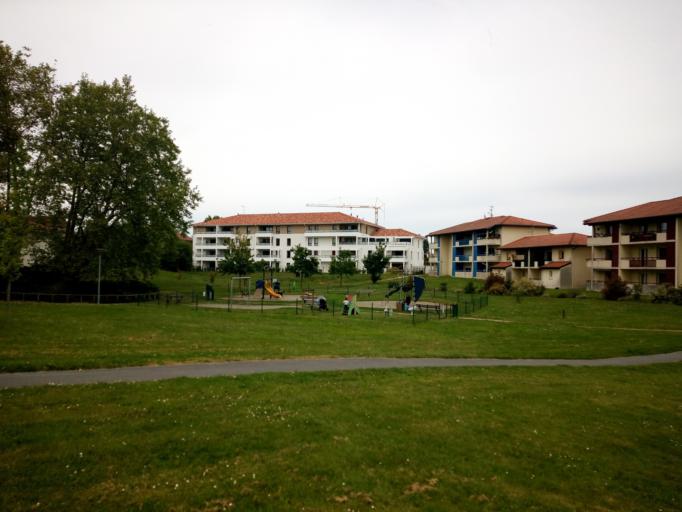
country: FR
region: Aquitaine
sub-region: Departement des Landes
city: Saint-Martin-de-Seignanx
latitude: 43.5418
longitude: -1.3849
